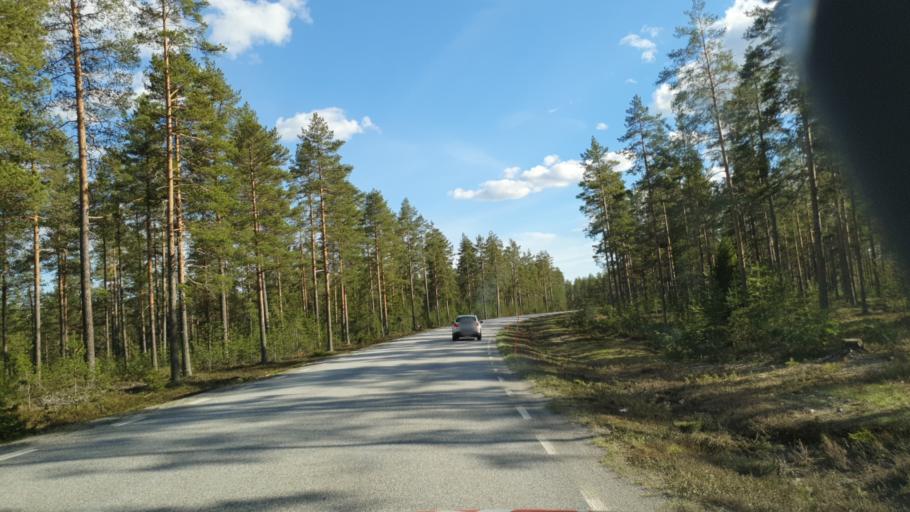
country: SE
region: Vaesterbotten
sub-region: Umea Kommun
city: Roback
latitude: 63.8960
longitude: 20.1583
